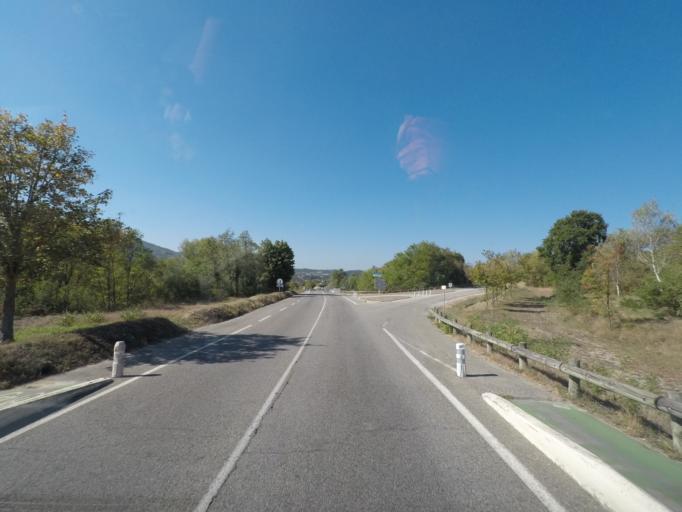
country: FR
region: Rhone-Alpes
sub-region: Departement de la Drome
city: Aouste-sur-Sye
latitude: 44.7040
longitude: 5.1130
